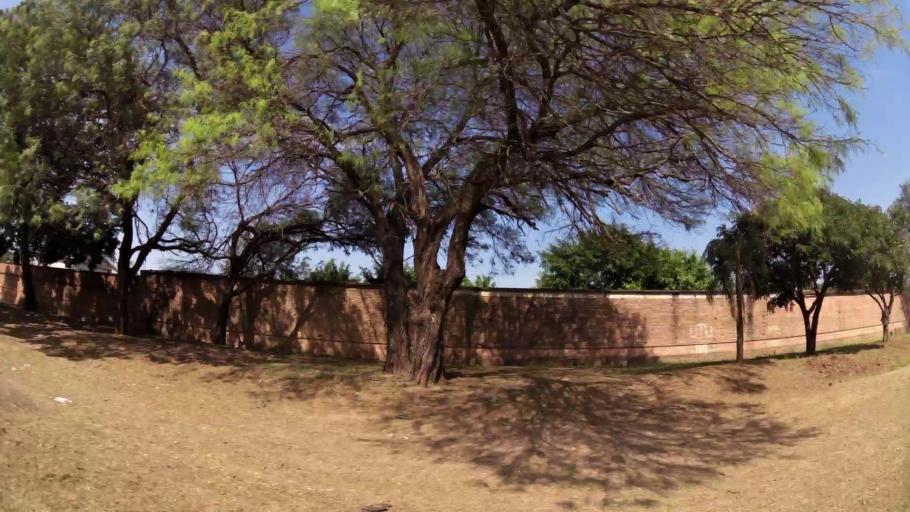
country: BO
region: Santa Cruz
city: Santa Cruz de la Sierra
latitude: -17.7473
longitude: -63.1602
